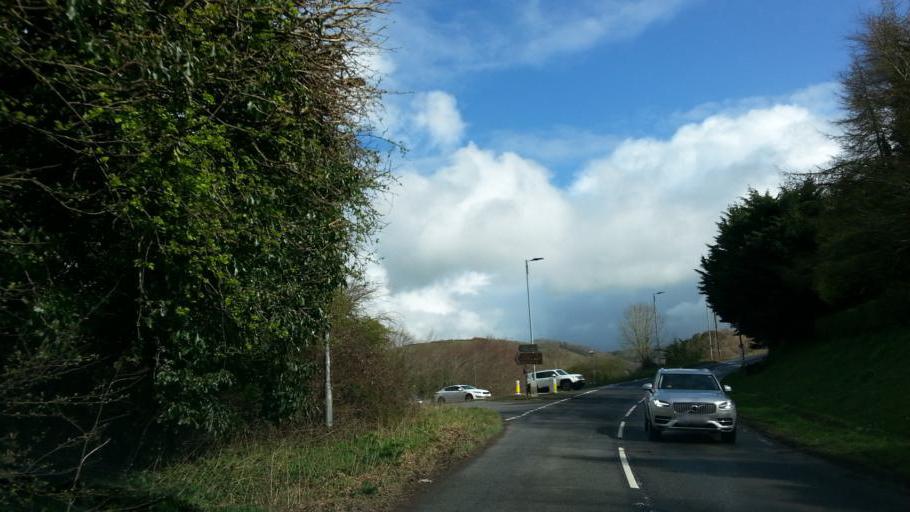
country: GB
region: England
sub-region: Devon
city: Barnstaple
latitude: 51.0983
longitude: -4.0549
